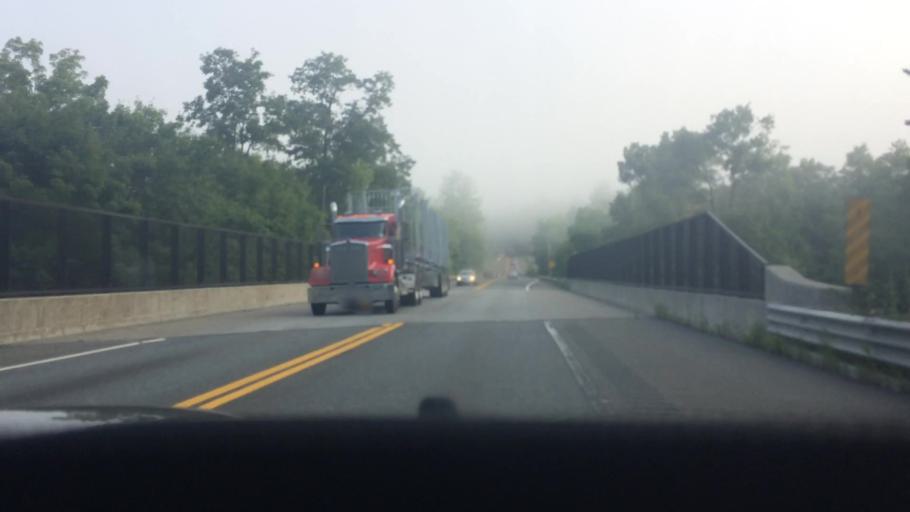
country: US
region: Massachusetts
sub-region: Franklin County
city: Millers Falls
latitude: 42.5889
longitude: -72.4901
